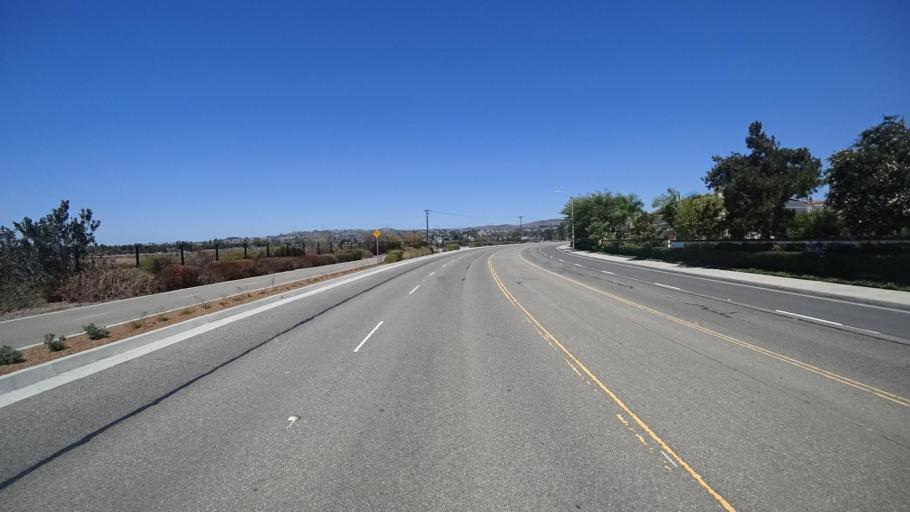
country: US
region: California
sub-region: Orange County
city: Villa Park
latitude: 33.8033
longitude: -117.8057
